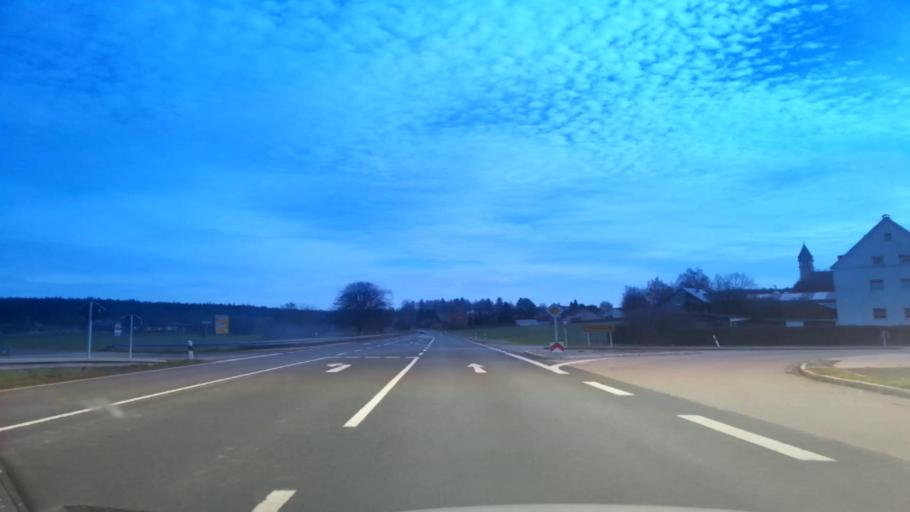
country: DE
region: Bavaria
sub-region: Upper Palatinate
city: Pechbrunn
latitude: 49.9735
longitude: 12.1637
